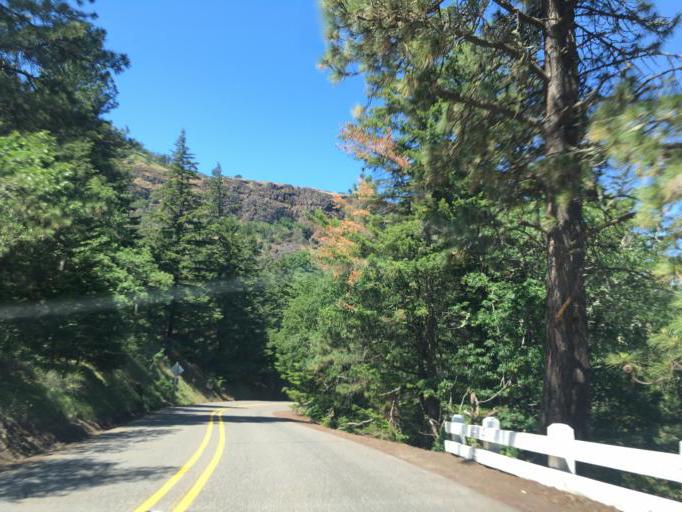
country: US
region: Oregon
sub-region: Wasco County
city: Chenoweth
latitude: 45.6761
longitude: -121.2948
